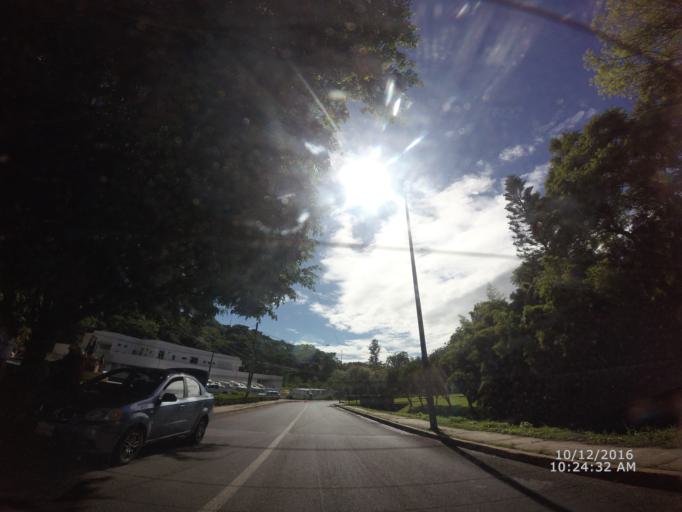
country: TR
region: Sivas
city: Karayun
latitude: 39.6709
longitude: 37.2625
